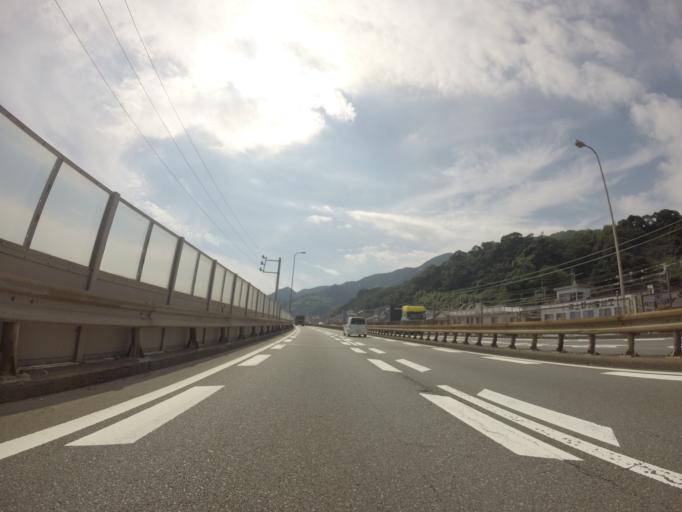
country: JP
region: Shizuoka
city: Fujinomiya
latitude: 35.1012
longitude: 138.5561
